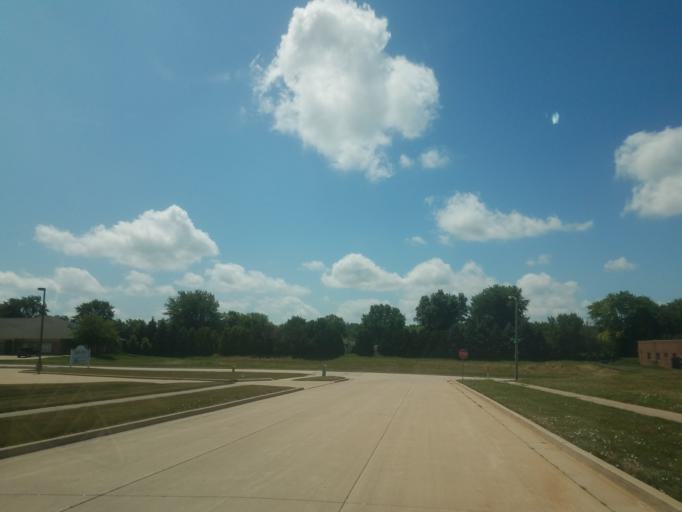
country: US
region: Illinois
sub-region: McLean County
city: Bloomington
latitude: 40.4820
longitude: -88.9411
